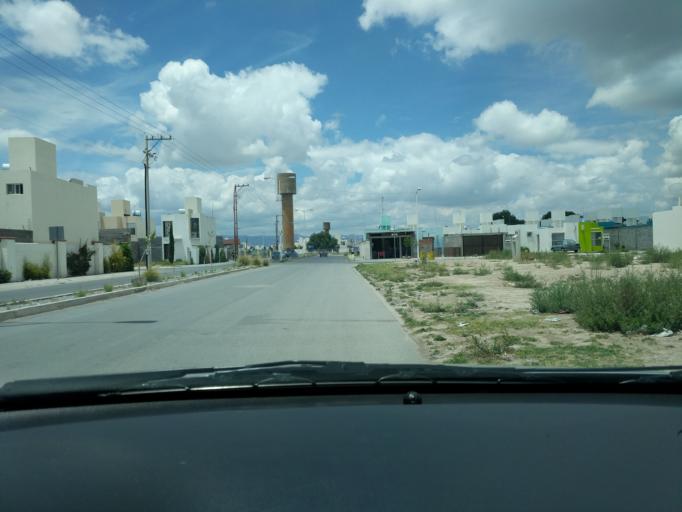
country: MX
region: San Luis Potosi
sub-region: San Luis Potosi
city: Fraccion Milpillas
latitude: 22.2205
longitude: -100.9345
